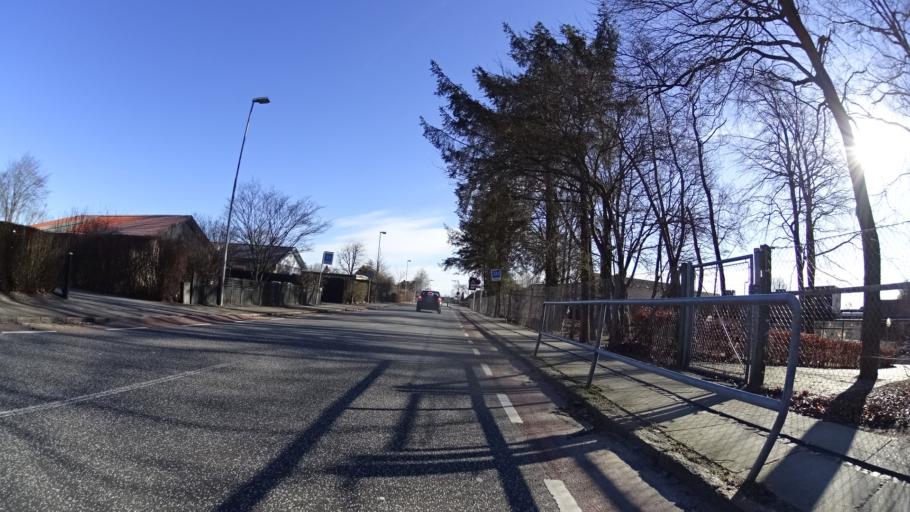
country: DK
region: Central Jutland
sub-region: Arhus Kommune
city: Kolt
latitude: 56.1072
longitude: 10.0944
